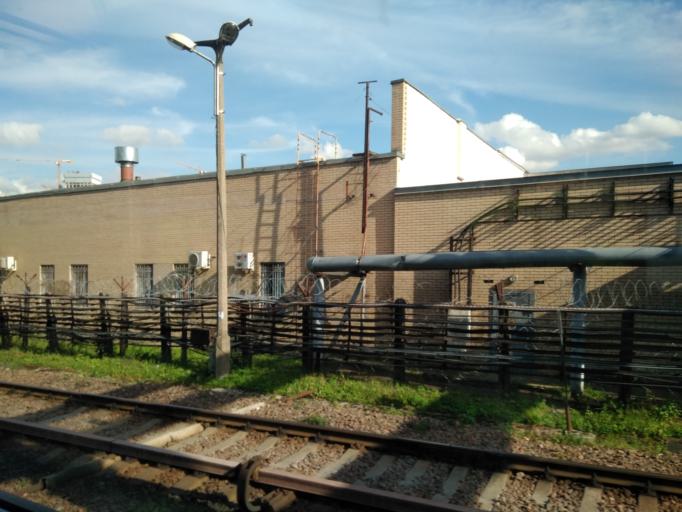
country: RU
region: Moskovskaya
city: Fili
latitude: 55.7445
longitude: 37.5004
